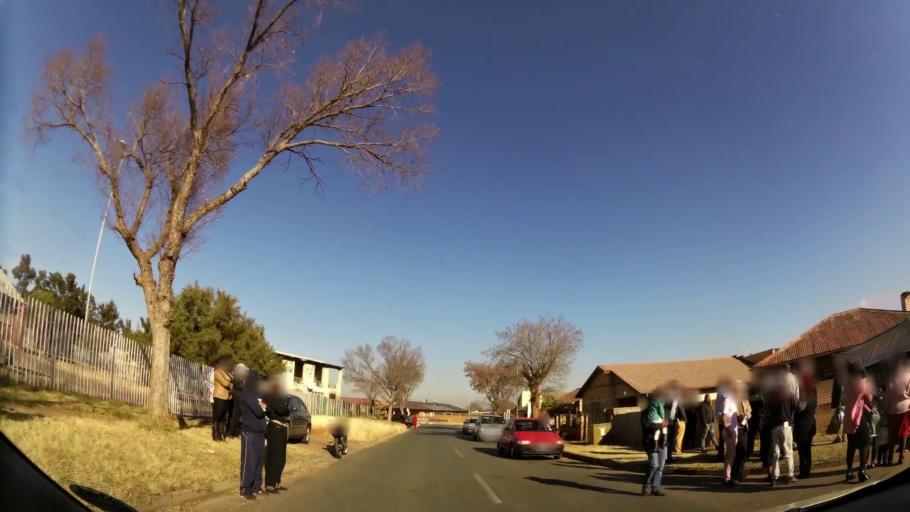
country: ZA
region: Gauteng
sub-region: City of Johannesburg Metropolitan Municipality
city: Roodepoort
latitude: -26.1542
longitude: 27.8521
